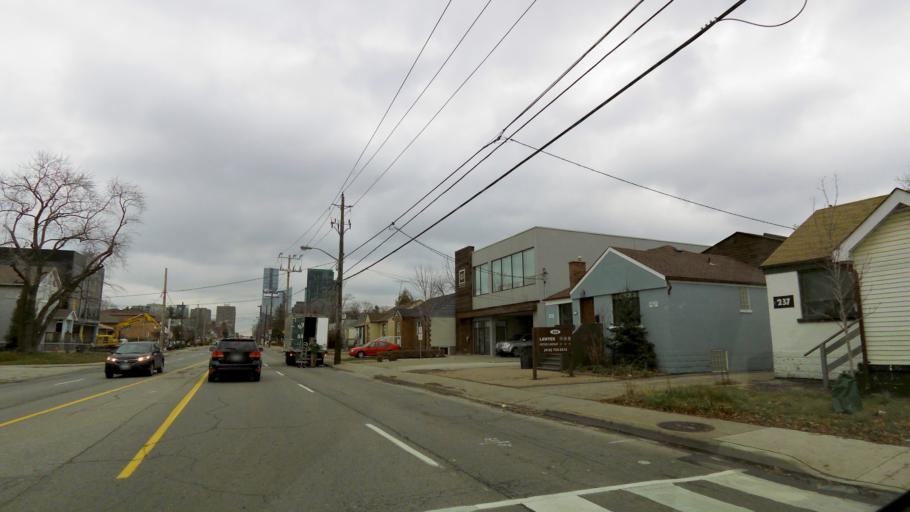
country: CA
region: Ontario
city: North York
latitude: 43.7589
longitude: -79.4226
